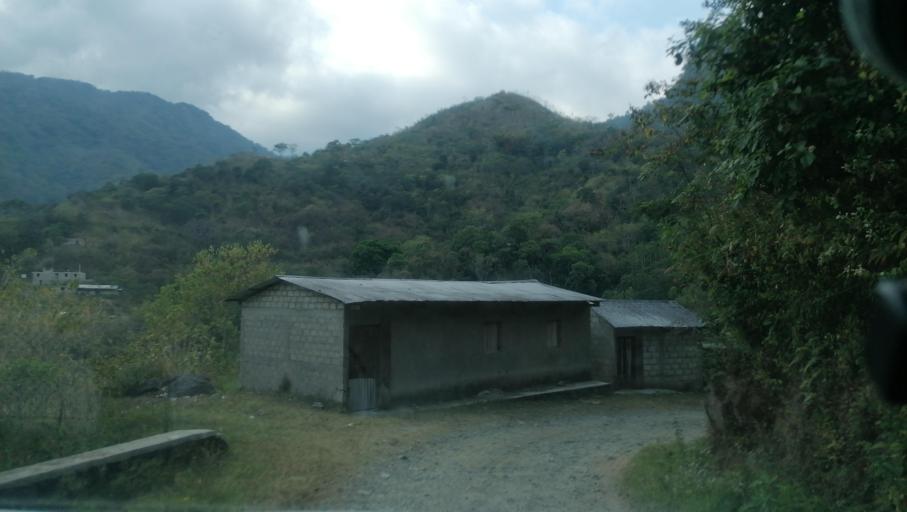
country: MX
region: Chiapas
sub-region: Cacahoatan
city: Benito Juarez
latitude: 15.1432
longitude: -92.1913
